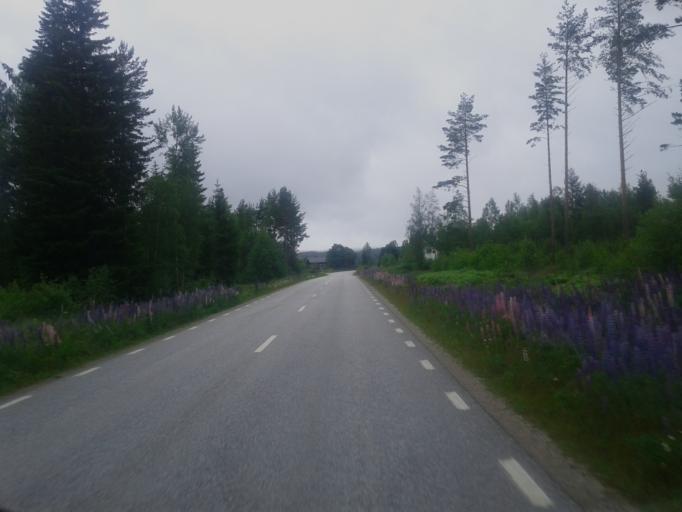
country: SE
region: Gaevleborg
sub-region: Nordanstigs Kommun
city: Bergsjoe
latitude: 61.9963
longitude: 17.0351
